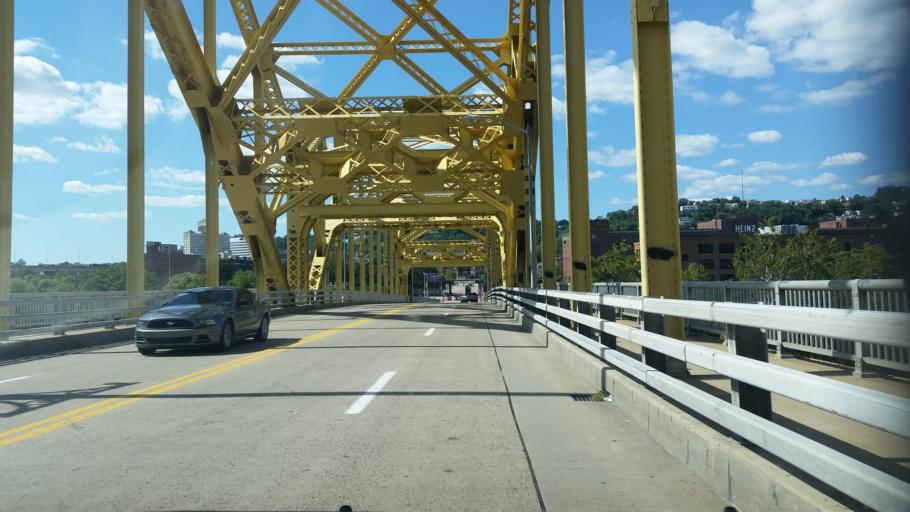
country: US
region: Pennsylvania
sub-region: Allegheny County
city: Pittsburgh
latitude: 40.4516
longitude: -79.9907
